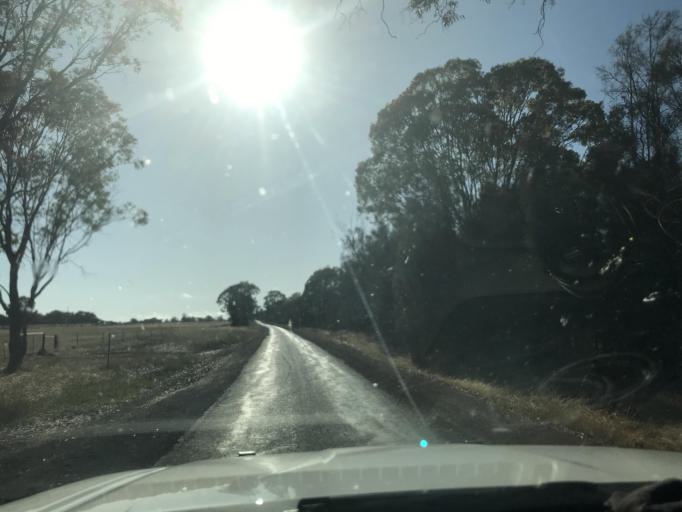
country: AU
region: Victoria
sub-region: Horsham
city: Horsham
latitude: -37.0044
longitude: 141.6145
